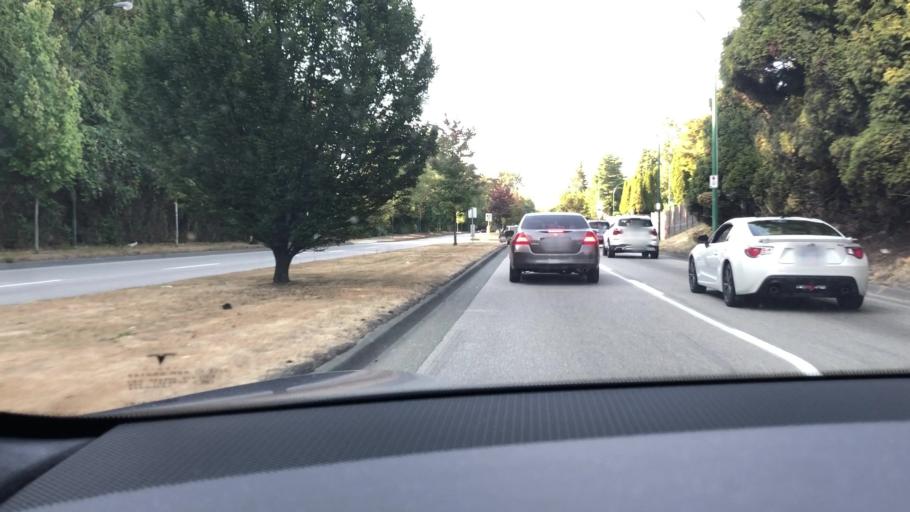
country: CA
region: British Columbia
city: Burnaby
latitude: 49.2195
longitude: -123.0237
